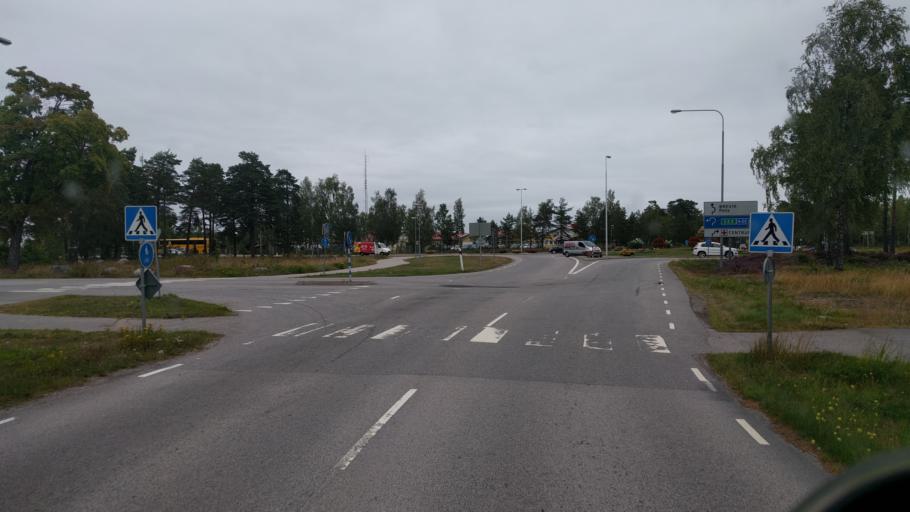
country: SE
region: Kalmar
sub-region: Vasterviks Kommun
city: Vaestervik
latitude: 57.7645
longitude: 16.5992
